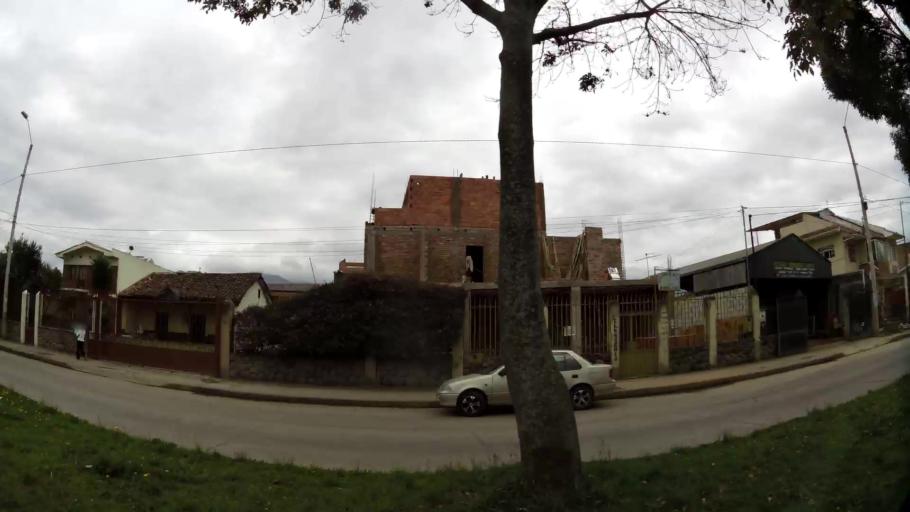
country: EC
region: Azuay
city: Cuenca
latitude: -2.9196
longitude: -79.0361
